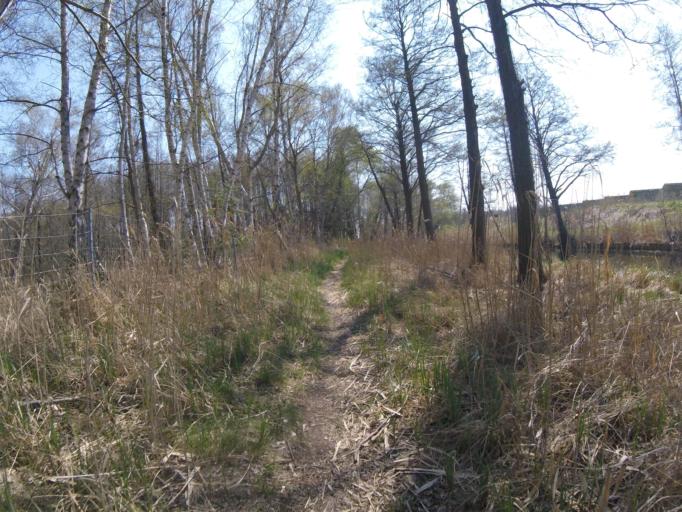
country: DE
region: Brandenburg
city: Mittenwalde
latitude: 52.2536
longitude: 13.5389
